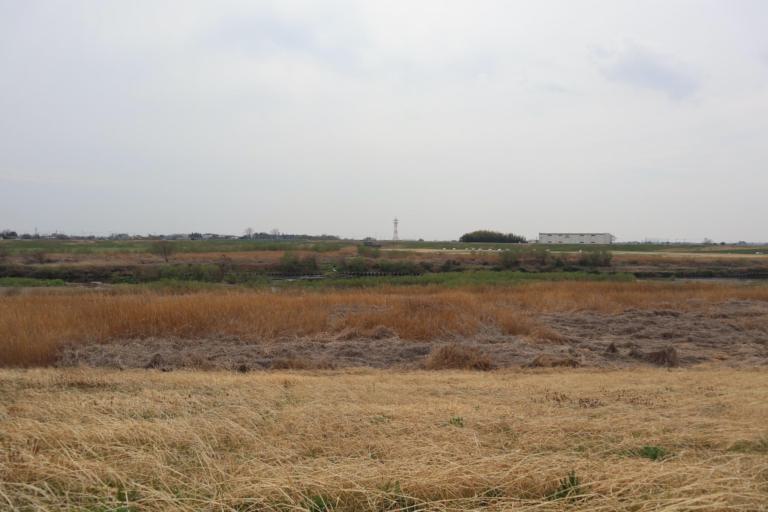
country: JP
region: Tochigi
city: Fujioka
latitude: 36.2666
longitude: 139.6378
